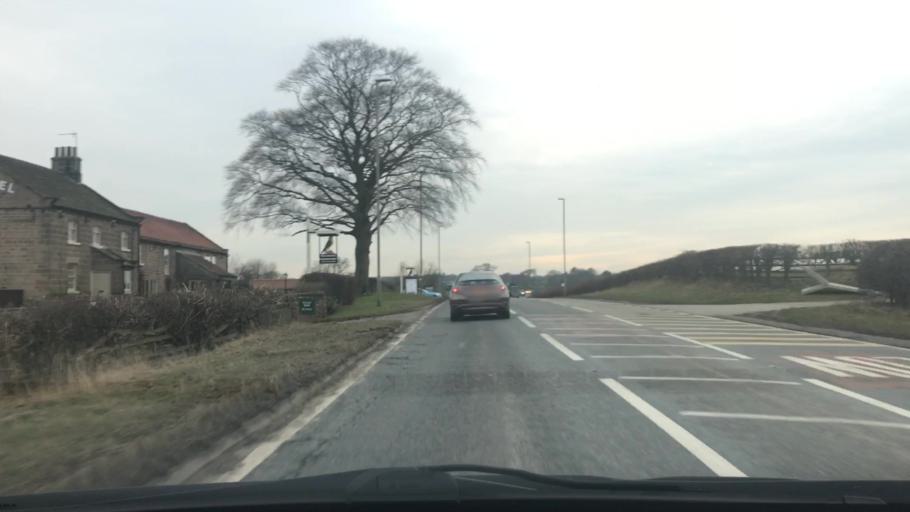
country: GB
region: England
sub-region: North Yorkshire
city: Knaresborough
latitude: 53.9807
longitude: -1.4748
